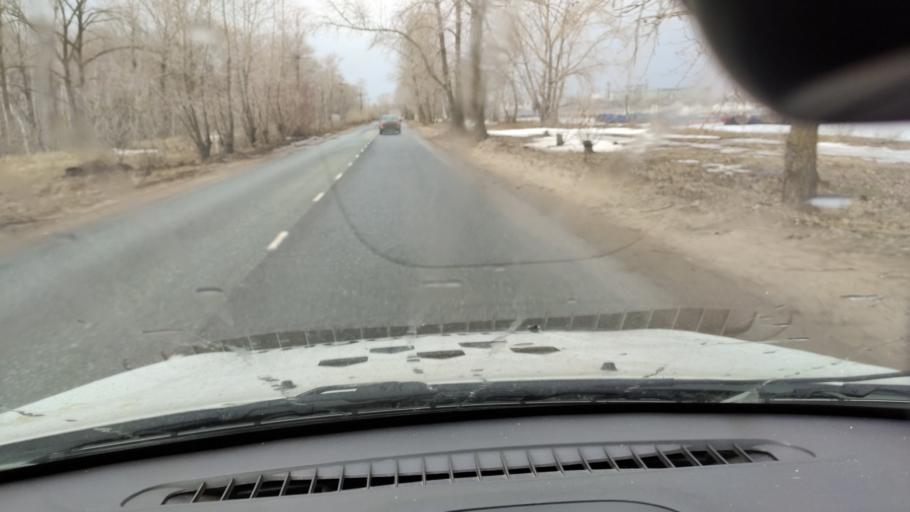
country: RU
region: Samara
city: Zhigulevsk
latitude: 53.4596
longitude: 49.5229
